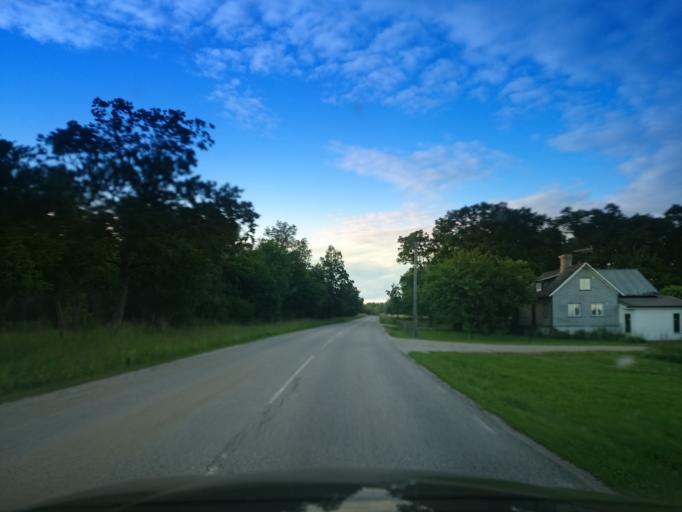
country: SE
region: Gotland
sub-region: Gotland
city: Hemse
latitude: 57.3100
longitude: 18.3803
